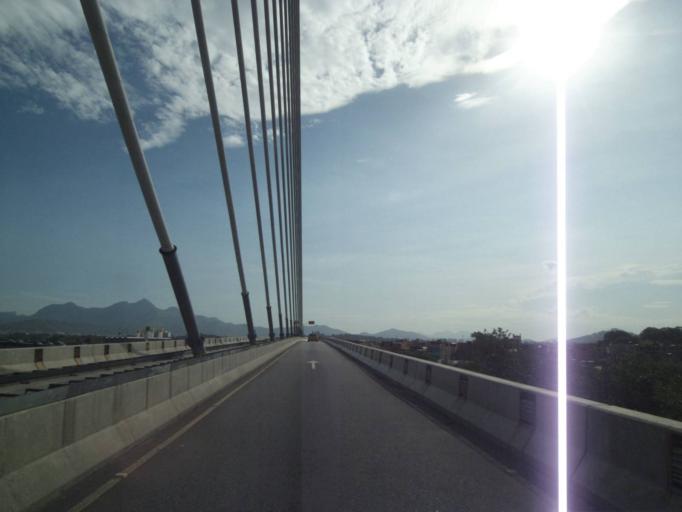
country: BR
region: Rio de Janeiro
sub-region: Rio De Janeiro
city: Rio de Janeiro
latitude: -22.8663
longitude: -43.2317
